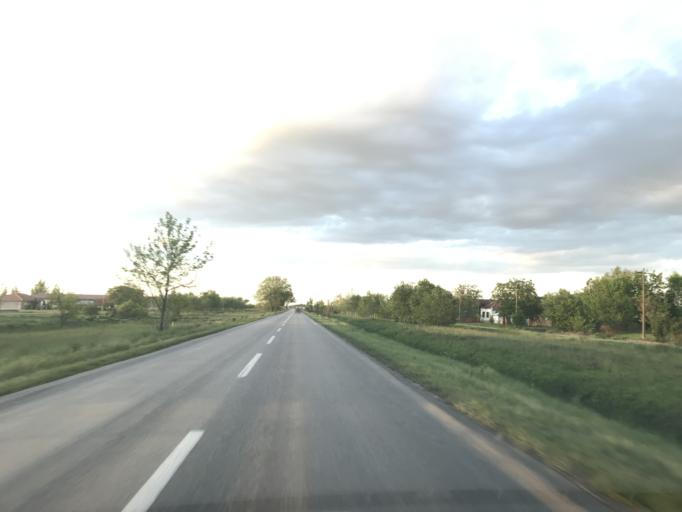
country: RS
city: Banatsko Karadordevo
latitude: 45.5936
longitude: 20.5585
